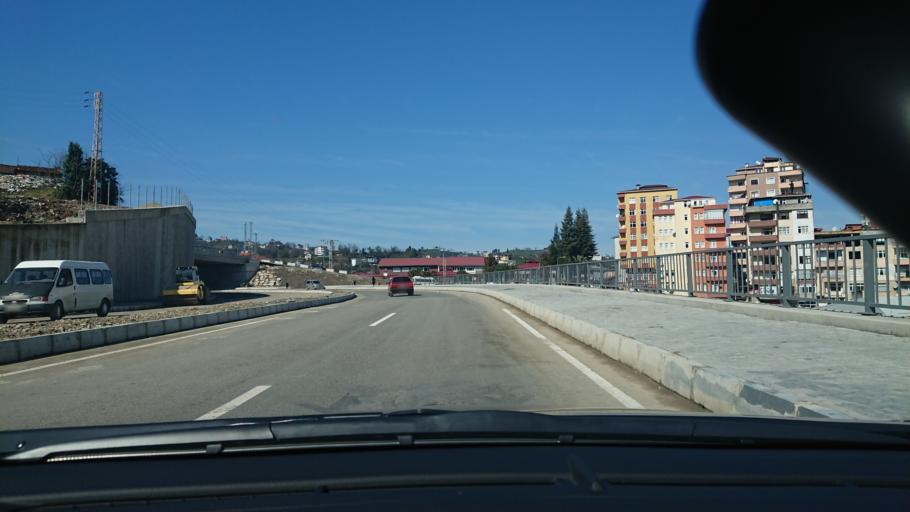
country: TR
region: Rize
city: Rize
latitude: 41.0152
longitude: 40.5129
